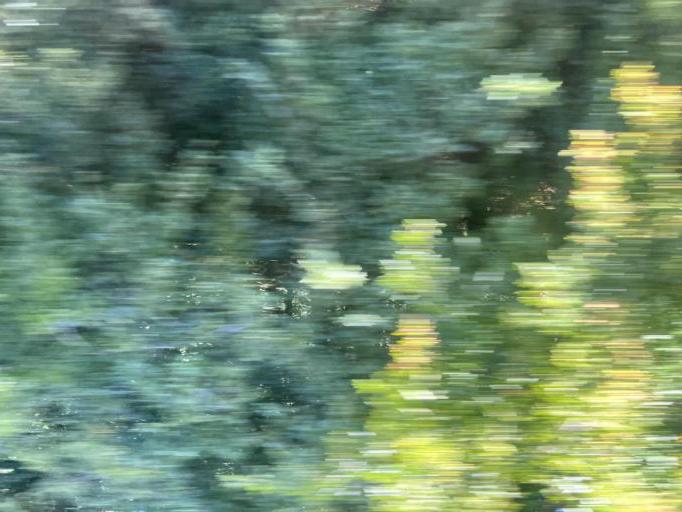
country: GB
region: England
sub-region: Lincolnshire
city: Wainfleet All Saints
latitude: 53.1352
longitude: 0.1895
